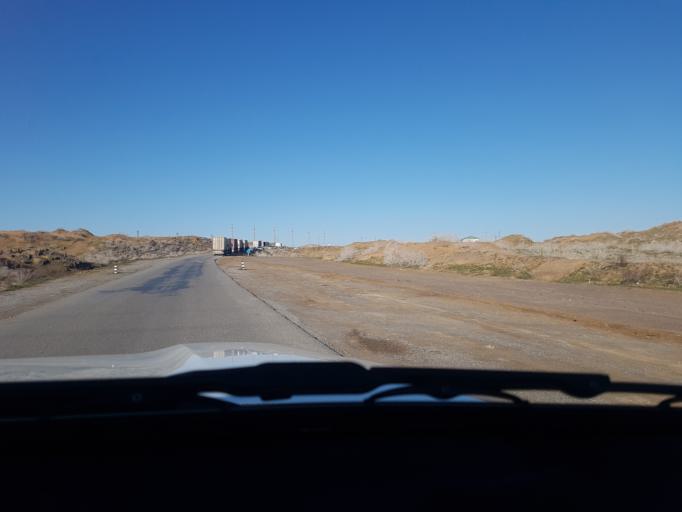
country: TM
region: Mary
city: Yoloeten
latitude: 37.0366
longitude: 62.4424
